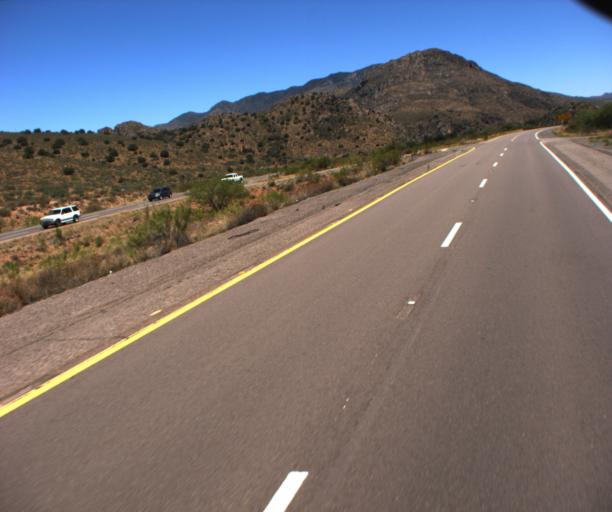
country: US
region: Arizona
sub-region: Gila County
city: Tonto Basin
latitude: 33.8559
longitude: -111.4729
